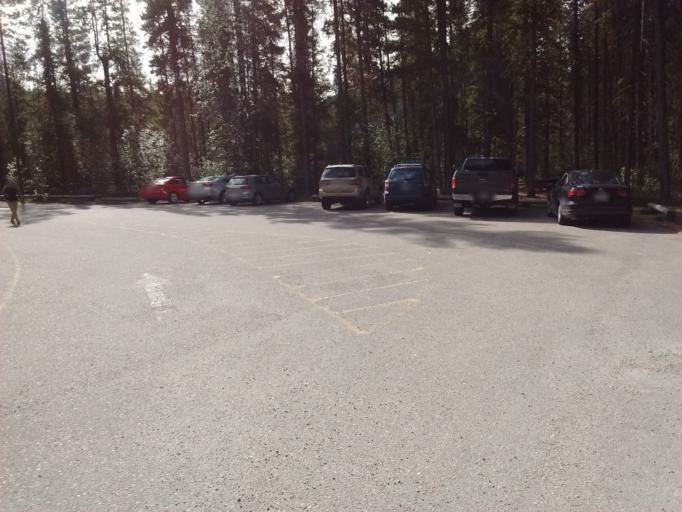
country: CA
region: Alberta
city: Jasper Park Lodge
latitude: 52.5327
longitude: -117.6462
